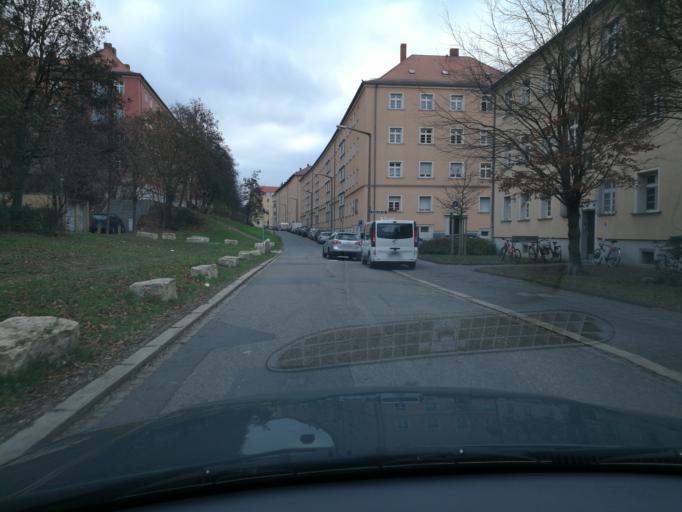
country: DE
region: Bavaria
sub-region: Regierungsbezirk Mittelfranken
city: Wetzendorf
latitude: 49.4602
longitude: 11.0507
